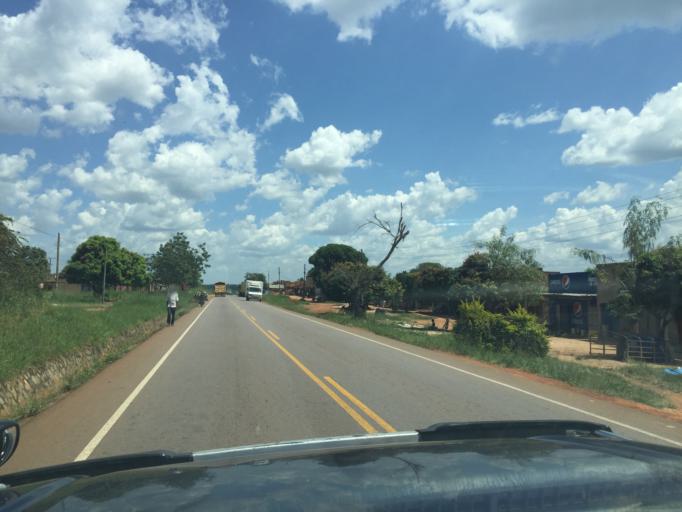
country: UG
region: Central Region
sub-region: Nakasongola District
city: Nakasongola
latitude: 1.3590
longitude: 32.3705
